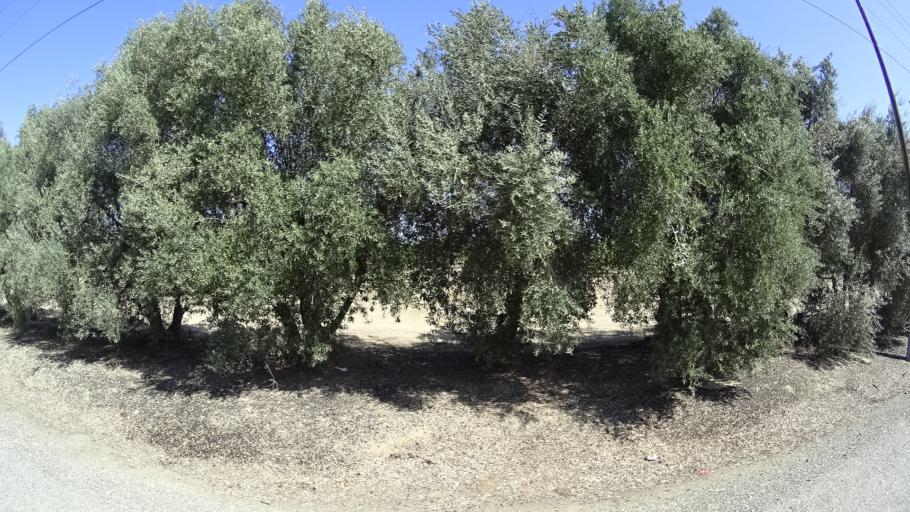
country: US
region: California
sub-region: Glenn County
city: Orland
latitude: 39.7106
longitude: -122.1283
